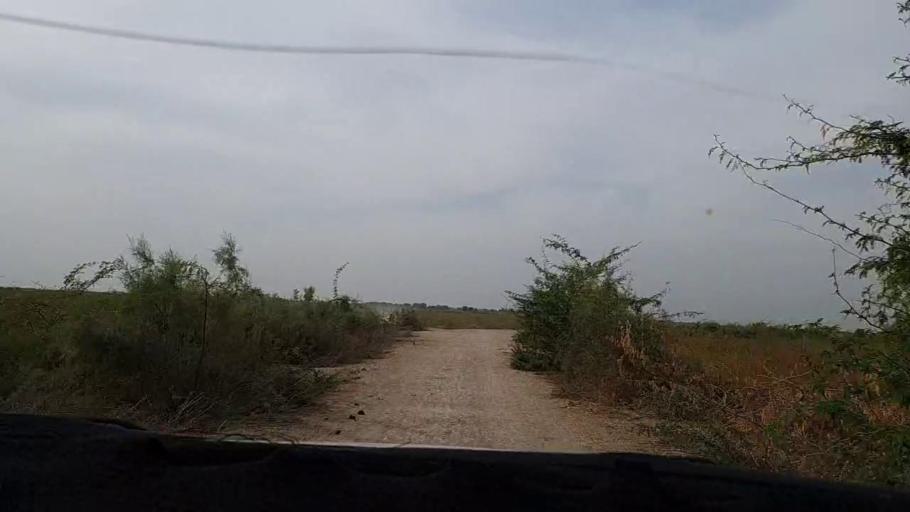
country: PK
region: Sindh
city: Pithoro
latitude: 25.5571
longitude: 69.3412
